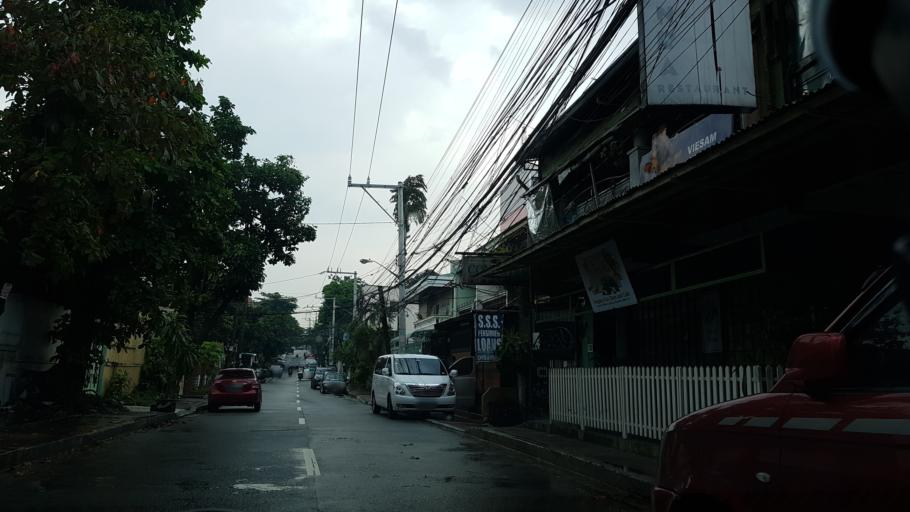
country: PH
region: Metro Manila
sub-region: Quezon City
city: Quezon City
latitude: 14.6439
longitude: 121.0502
